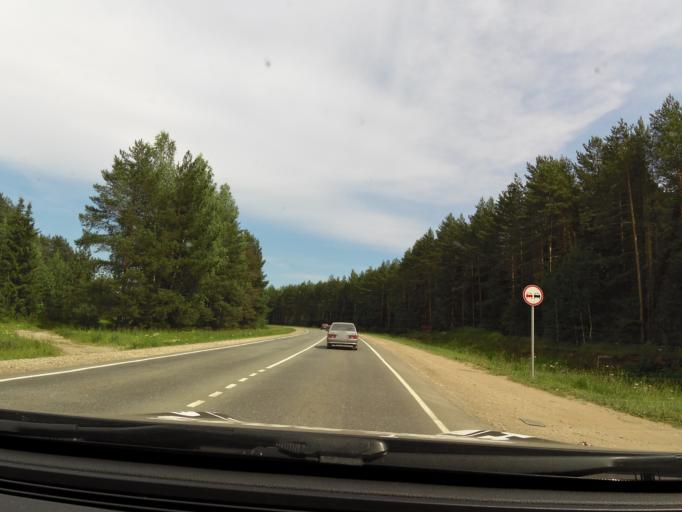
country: RU
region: Kirov
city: Vakhrushi
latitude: 58.6513
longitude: 49.8838
